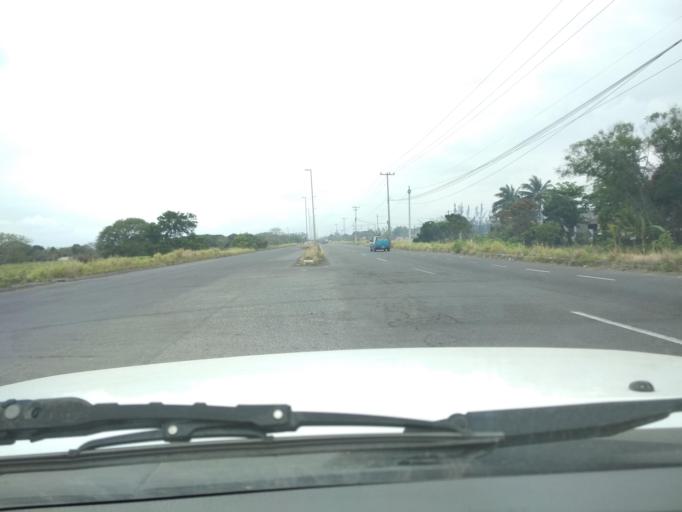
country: MX
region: Veracruz
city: Paso del Toro
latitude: 19.0620
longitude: -96.1318
